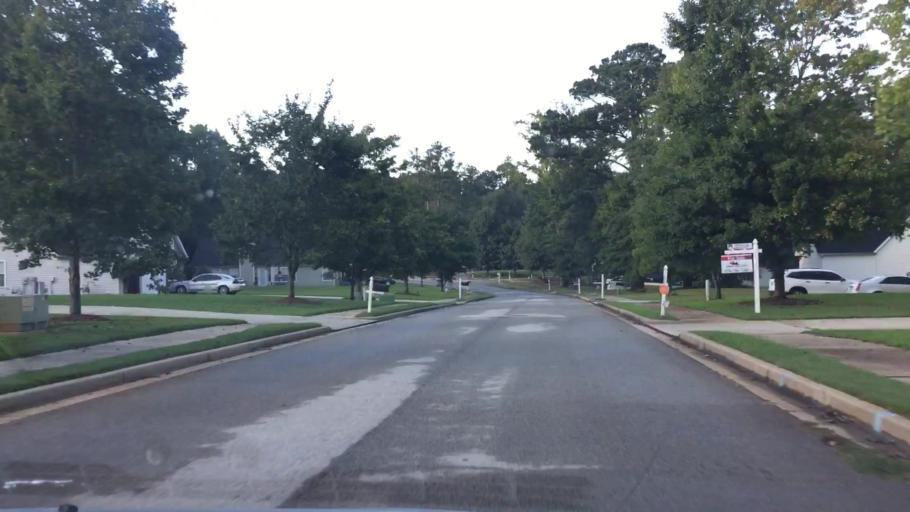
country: US
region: Georgia
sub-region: Henry County
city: Hampton
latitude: 33.4133
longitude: -84.2845
